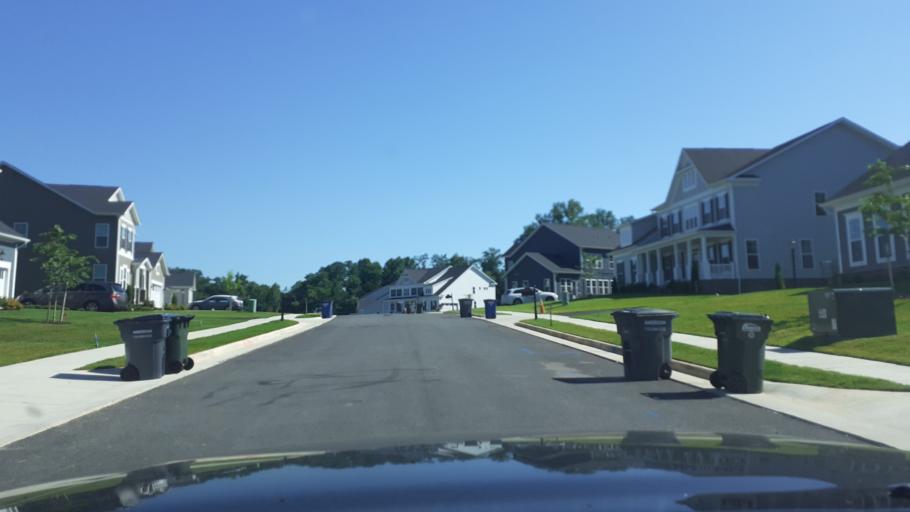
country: US
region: Virginia
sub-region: Fairfax County
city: Mantua
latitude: 38.8630
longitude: -77.2542
